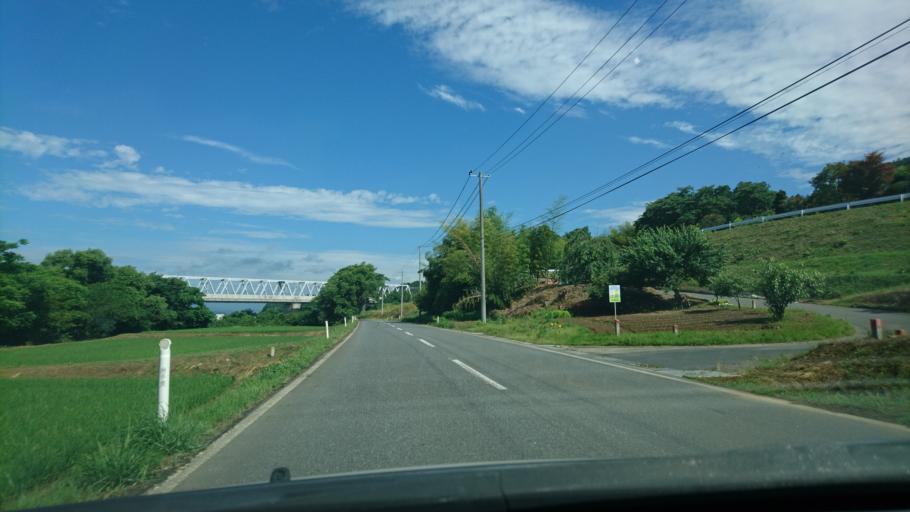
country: JP
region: Iwate
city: Ichinoseki
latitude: 38.9736
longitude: 141.1597
